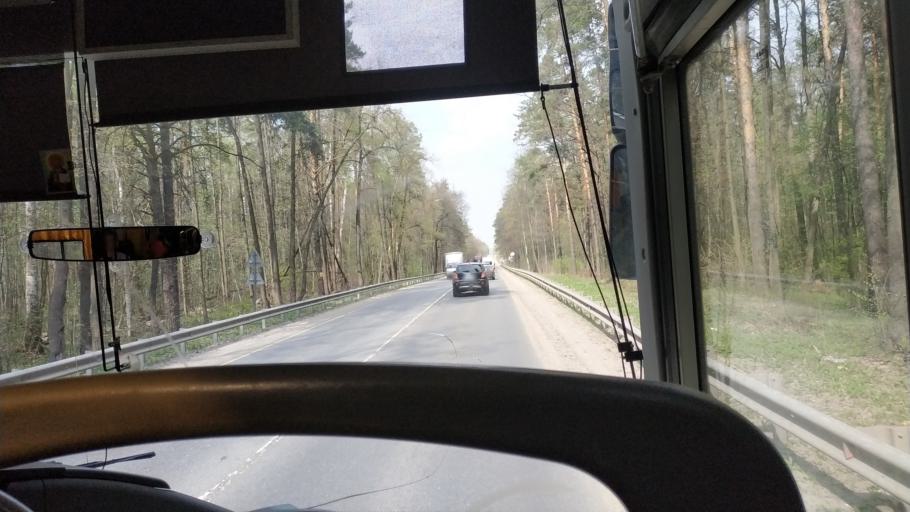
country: RU
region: Moskovskaya
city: Lytkarino
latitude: 55.6003
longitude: 37.9145
